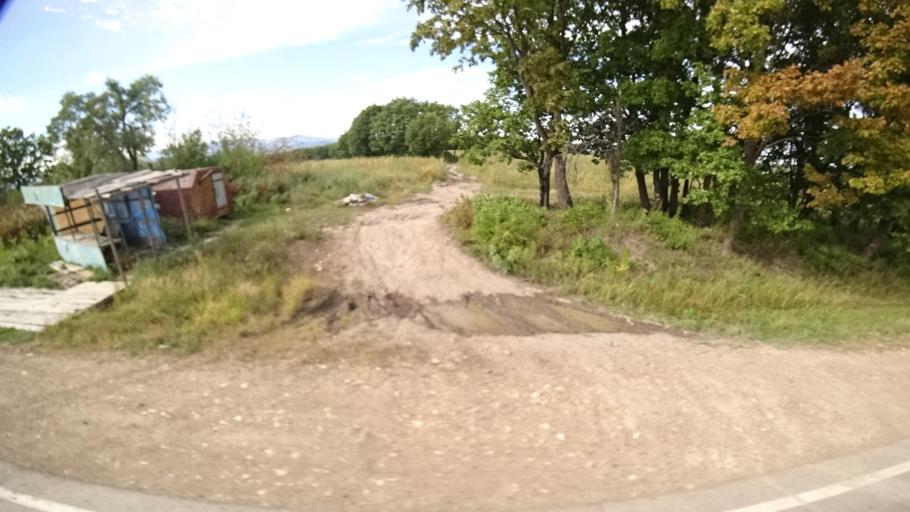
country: RU
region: Primorskiy
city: Dostoyevka
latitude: 44.3187
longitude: 133.4698
